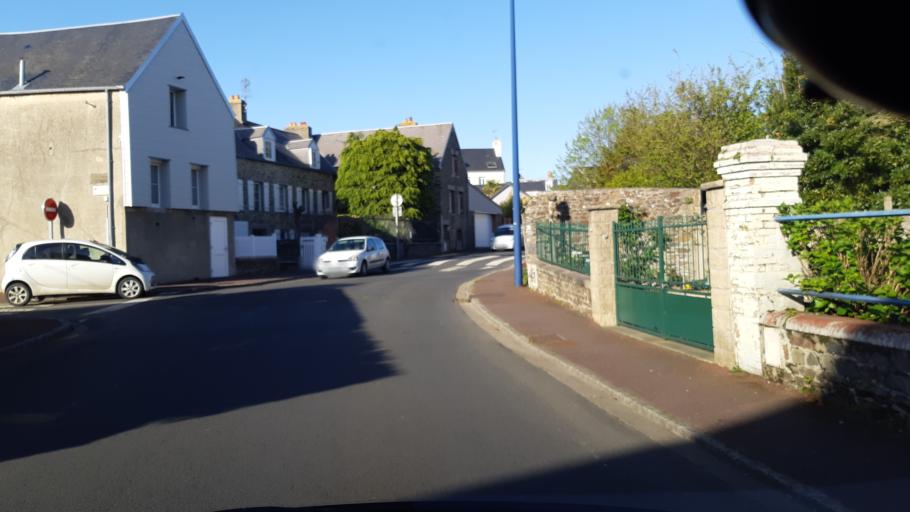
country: FR
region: Lower Normandy
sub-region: Departement de la Manche
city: Donville-les-Bains
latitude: 48.8349
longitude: -1.5811
